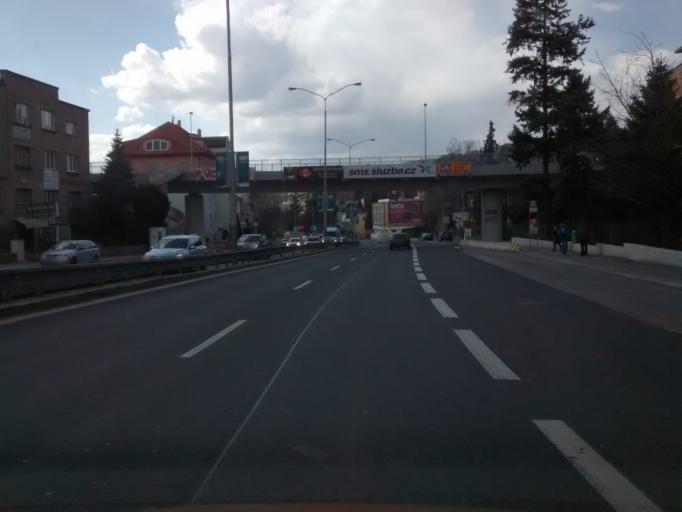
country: CZ
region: Praha
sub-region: Praha 8
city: Liben
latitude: 50.1175
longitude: 14.4574
